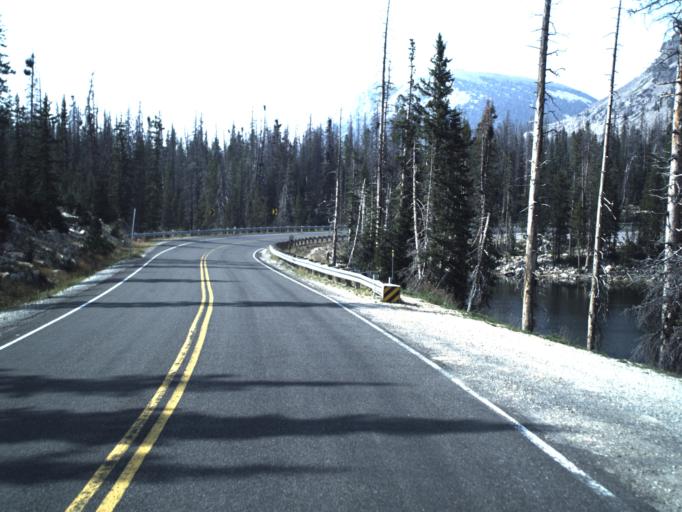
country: US
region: Utah
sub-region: Summit County
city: Kamas
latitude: 40.7109
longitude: -110.8939
